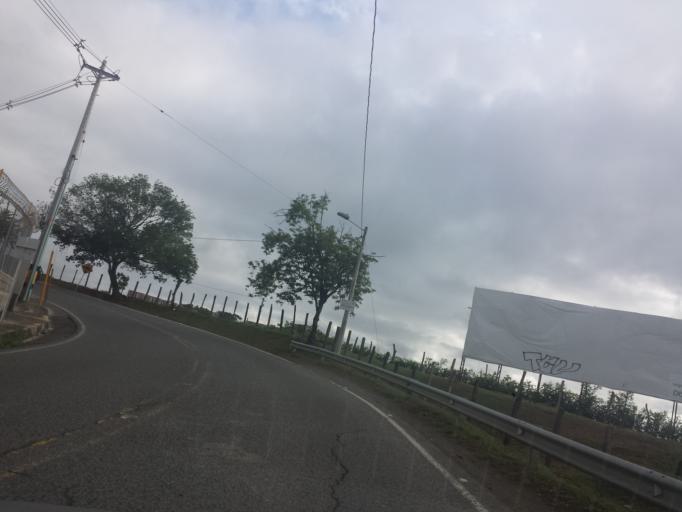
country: CO
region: Antioquia
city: Antioquia
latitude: 6.5528
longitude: -75.8208
